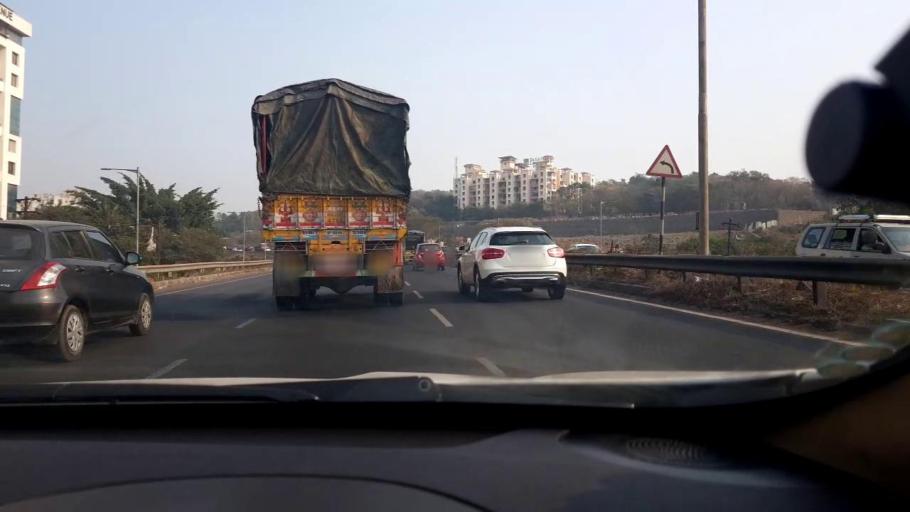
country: IN
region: Maharashtra
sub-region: Pune Division
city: Kharakvasla
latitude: 18.5105
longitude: 73.7727
